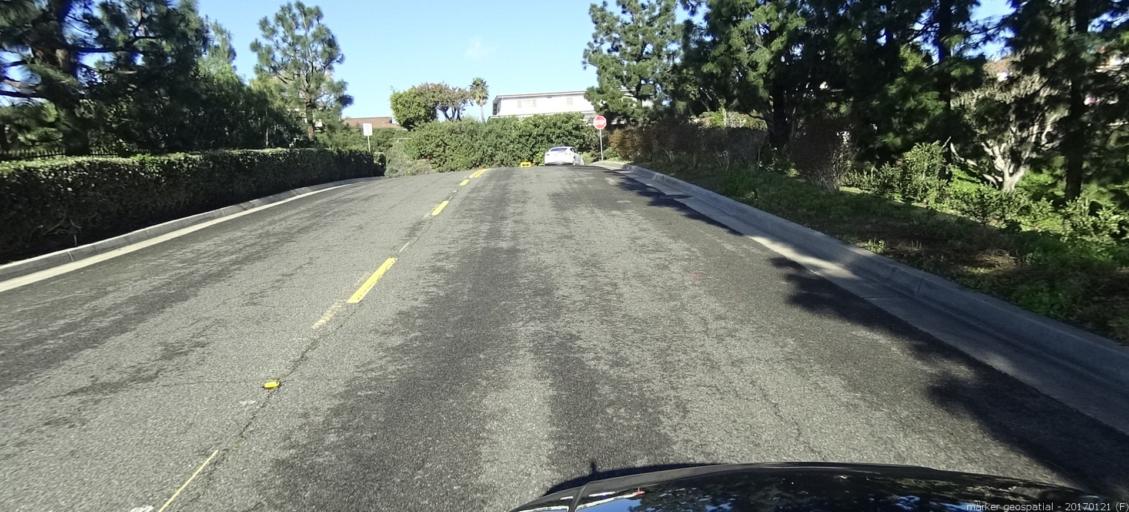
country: US
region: California
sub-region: Orange County
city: North Tustin
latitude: 33.7653
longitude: -117.7796
